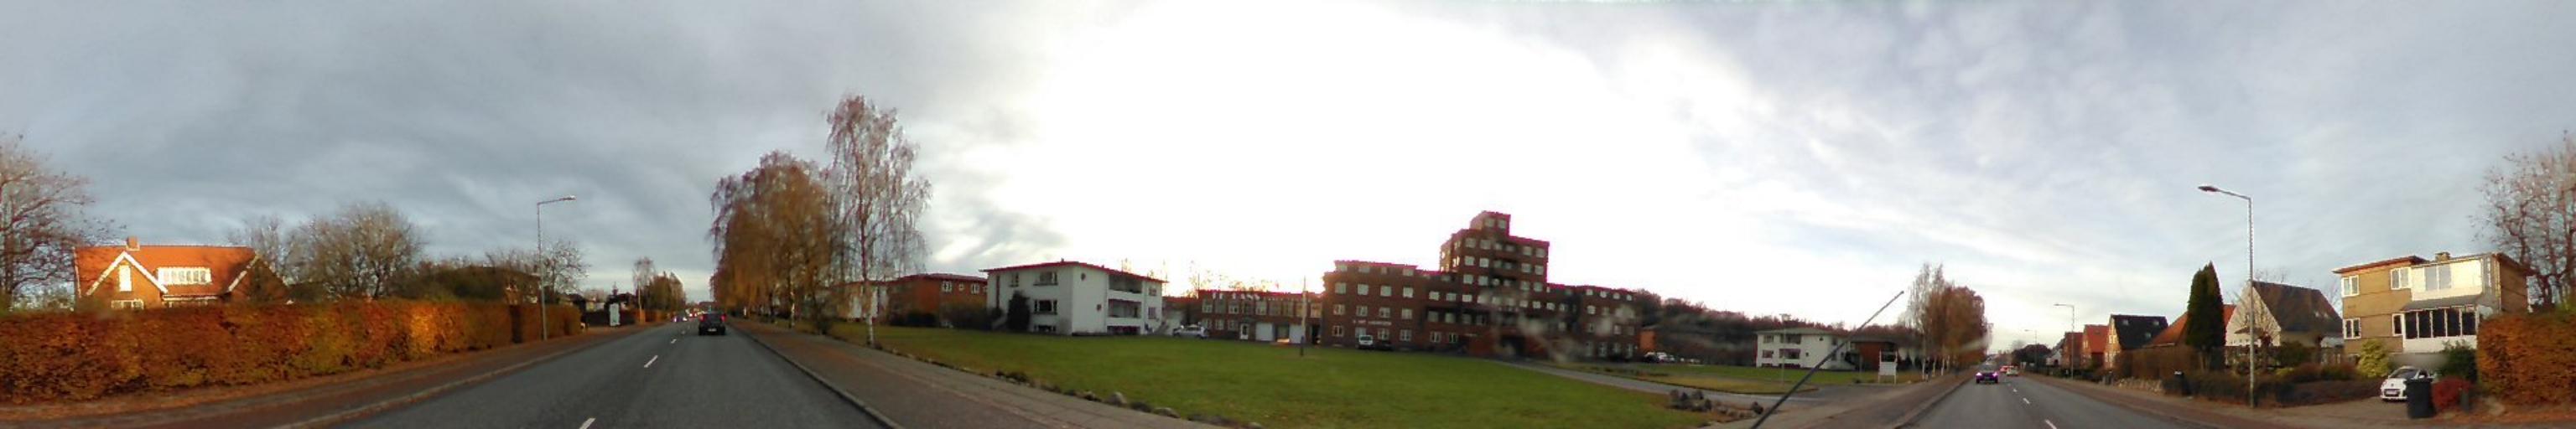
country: DK
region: South Denmark
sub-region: Vejle Kommune
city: Vejle
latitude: 55.6911
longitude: 9.5489
